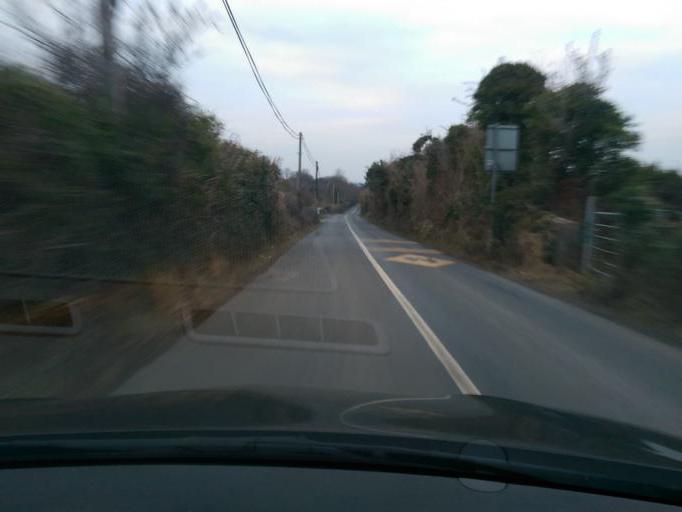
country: IE
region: Connaught
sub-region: County Galway
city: Moycullen
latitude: 53.3077
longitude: -9.1521
